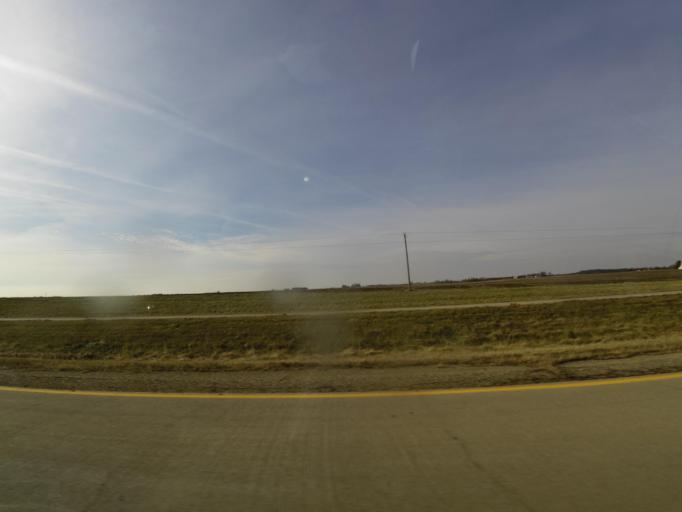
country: US
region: Illinois
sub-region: McLean County
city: Heyworth
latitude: 40.2949
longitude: -88.9777
